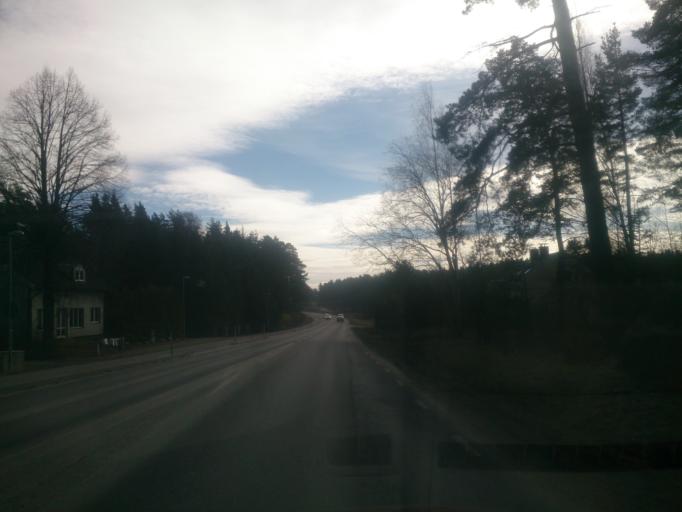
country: SE
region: OEstergoetland
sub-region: Norrkopings Kommun
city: Kimstad
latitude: 58.5547
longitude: 15.9548
